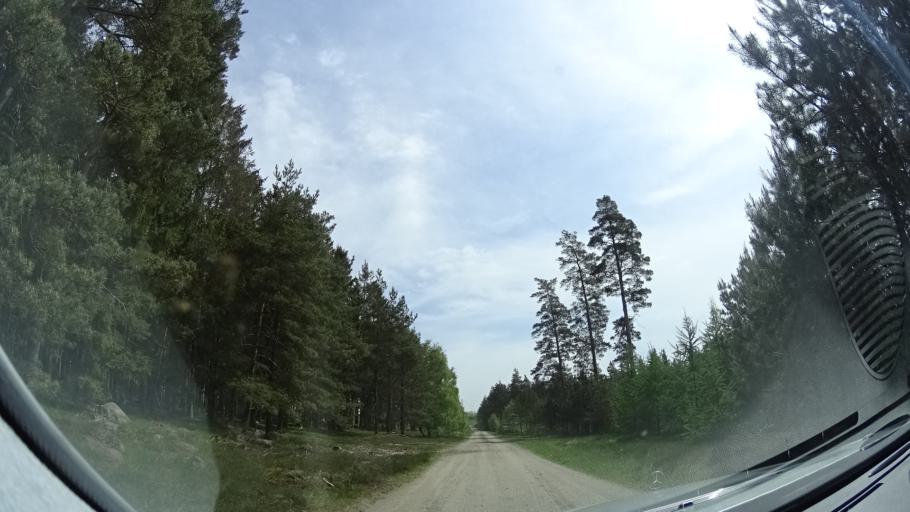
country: SE
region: Skane
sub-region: Sjobo Kommun
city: Sjoebo
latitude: 55.6679
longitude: 13.6478
